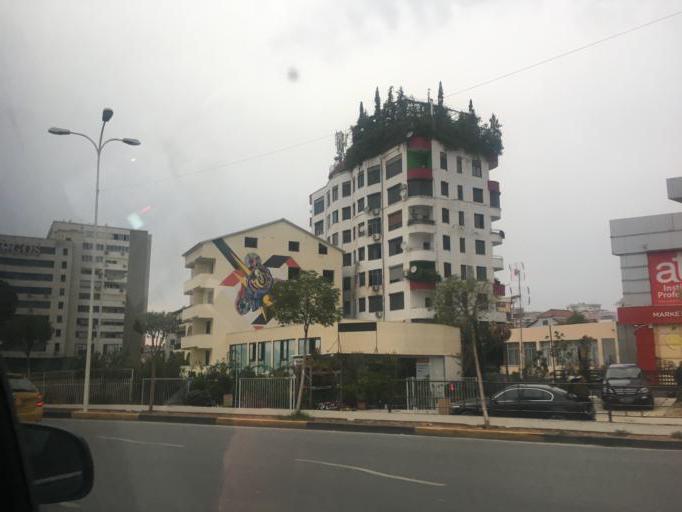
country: AL
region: Tirane
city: Tirana
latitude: 41.3333
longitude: 19.8045
